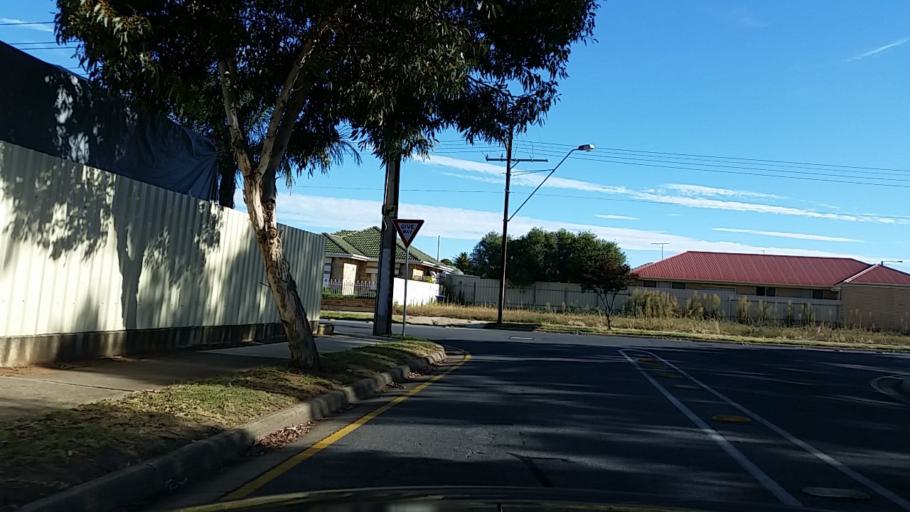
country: AU
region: South Australia
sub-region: Charles Sturt
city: Woodville West
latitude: -34.8876
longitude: 138.5227
